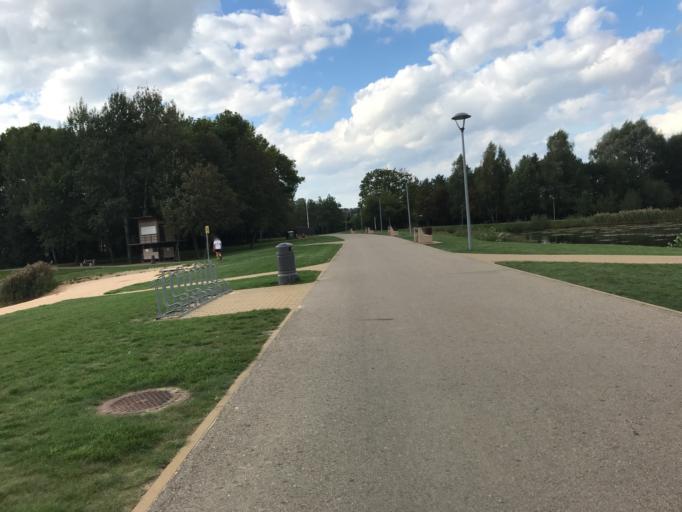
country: LT
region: Alytaus apskritis
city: Druskininkai
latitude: 54.0156
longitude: 23.9666
